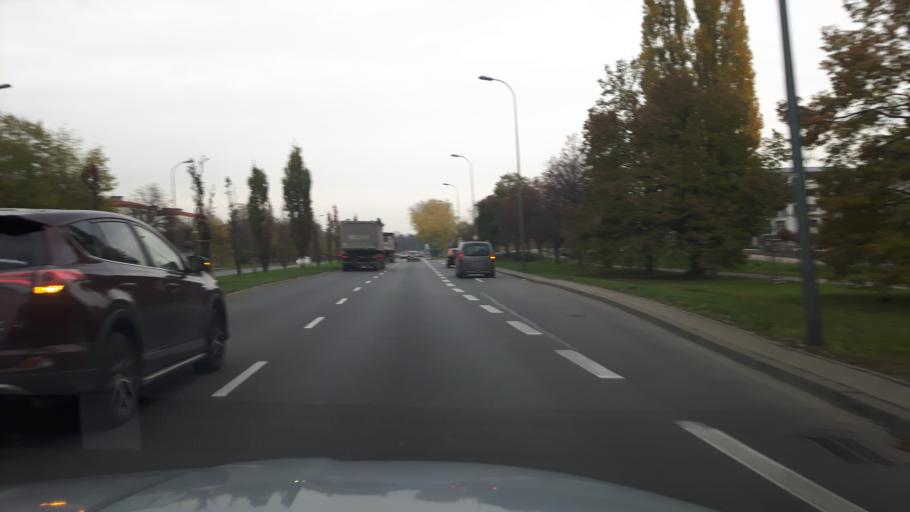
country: PL
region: Masovian Voivodeship
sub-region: Warszawa
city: Wilanow
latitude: 52.1674
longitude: 21.0779
